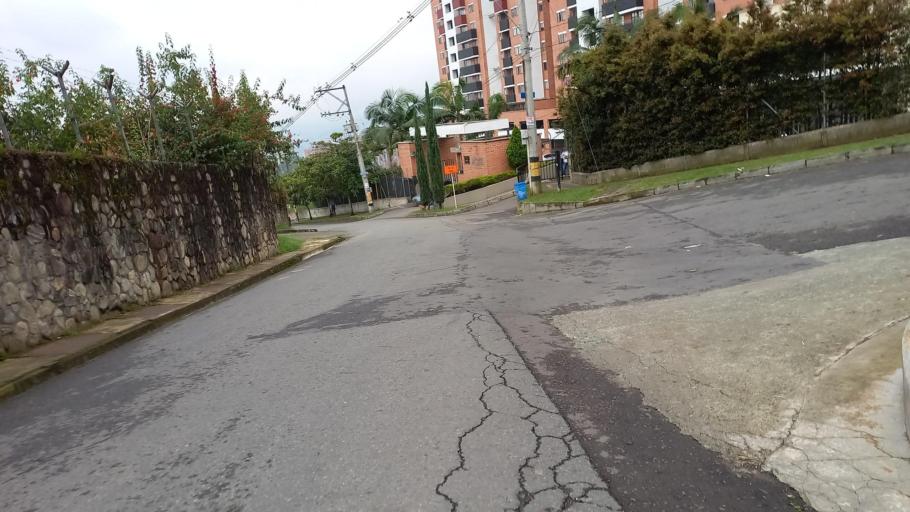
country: CO
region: Antioquia
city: La Estrella
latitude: 6.1655
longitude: -75.6469
